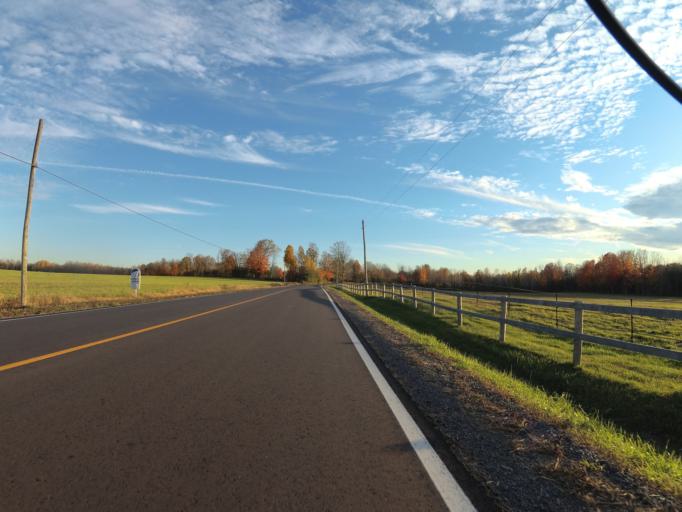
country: CA
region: Ontario
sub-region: Lanark County
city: Smiths Falls
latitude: 44.9520
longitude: -75.8152
